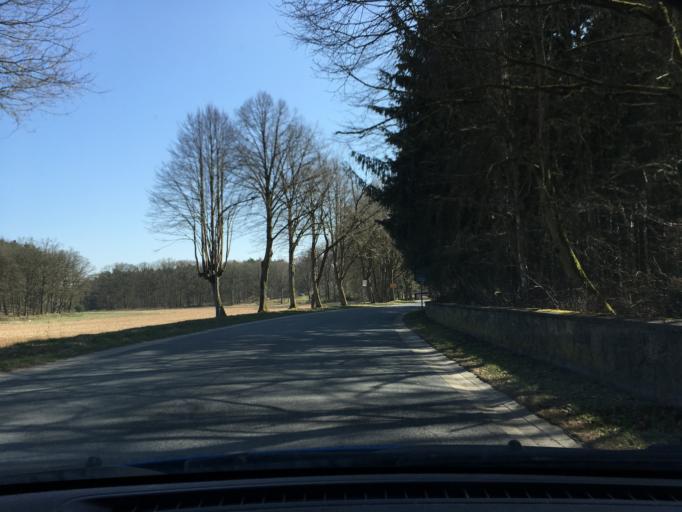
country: DE
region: Lower Saxony
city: Wriedel
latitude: 53.0731
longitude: 10.2841
